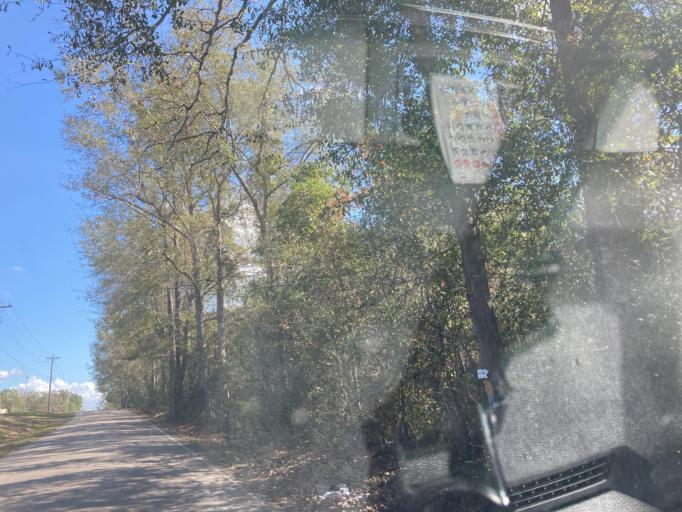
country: US
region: Mississippi
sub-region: Lamar County
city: Purvis
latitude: 31.2295
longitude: -89.4242
